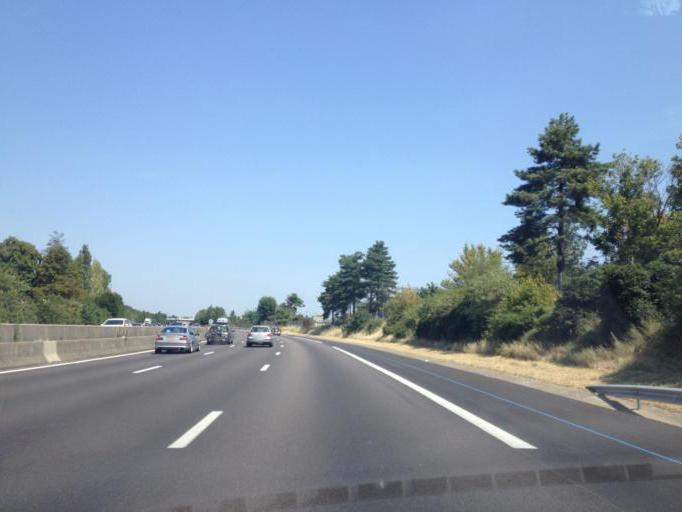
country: FR
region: Rhone-Alpes
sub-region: Departement de la Drome
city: Valence
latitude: 44.9470
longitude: 4.8909
